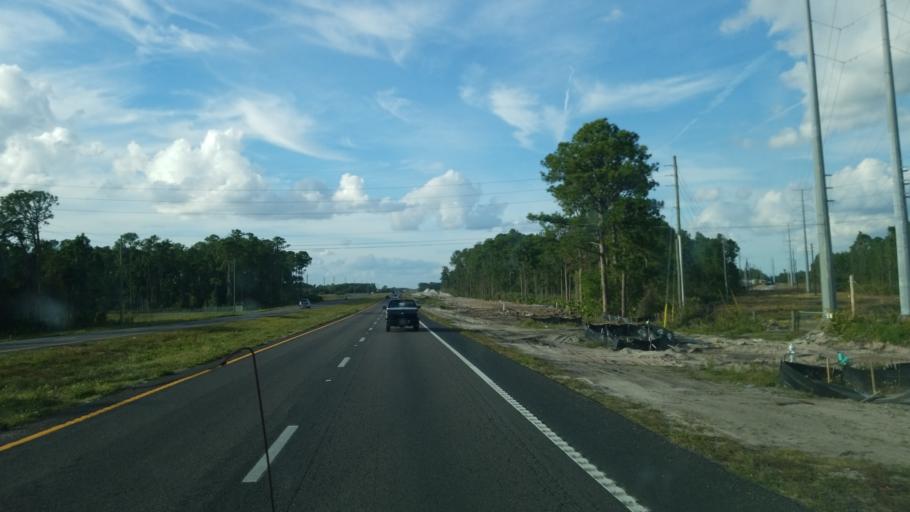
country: US
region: Florida
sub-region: Osceola County
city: Saint Cloud
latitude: 28.2179
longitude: -81.1777
